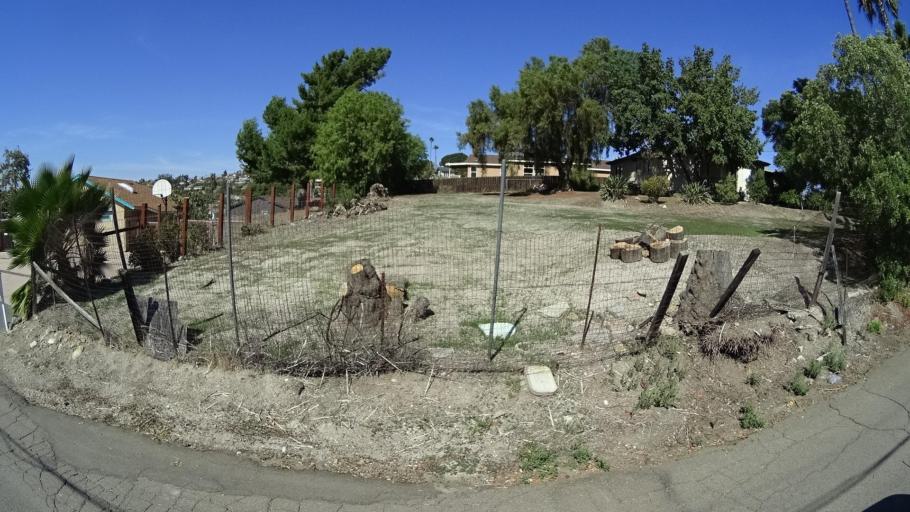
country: US
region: California
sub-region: San Diego County
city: Casa de Oro-Mount Helix
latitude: 32.7500
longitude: -116.9774
